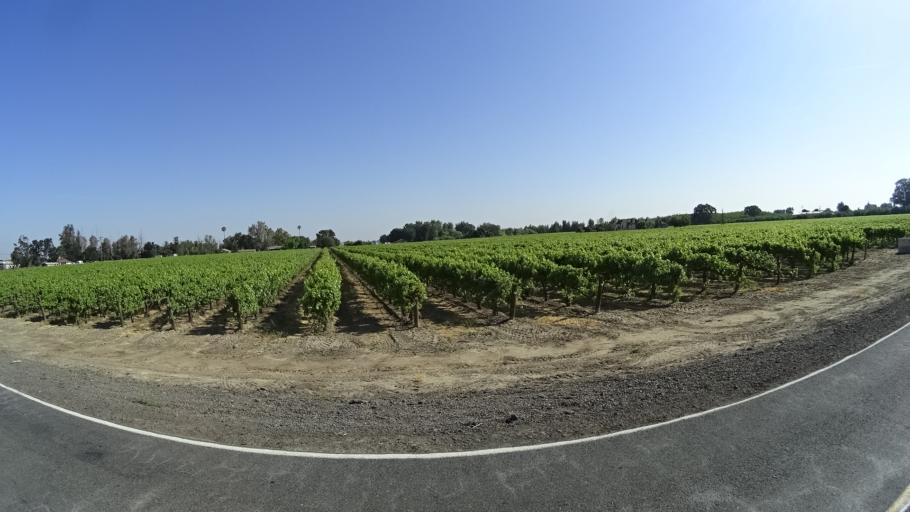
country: US
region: California
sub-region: Fresno County
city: Riverdale
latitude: 36.3651
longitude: -119.8241
